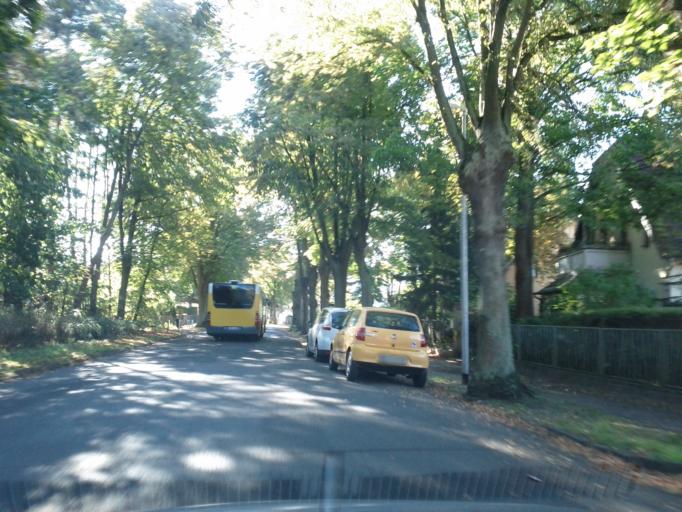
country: DE
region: Brandenburg
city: Schoneiche
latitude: 52.4606
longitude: 13.7031
